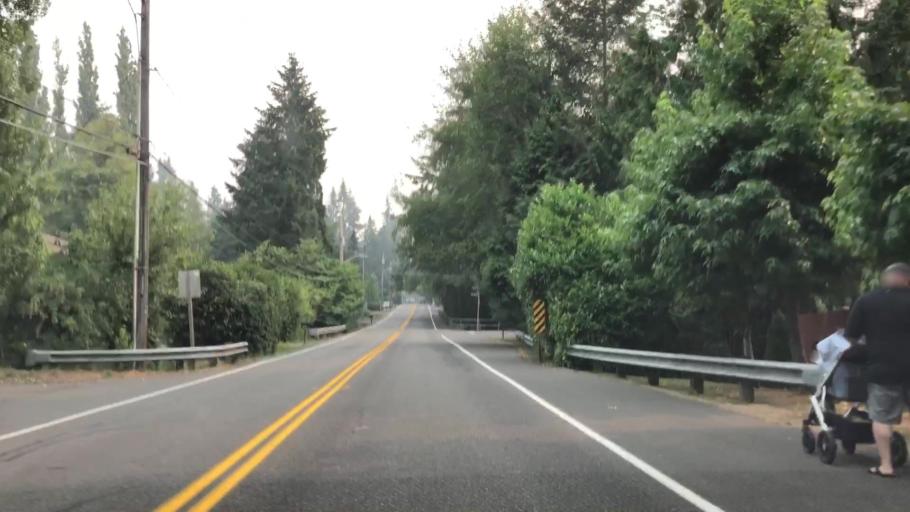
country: US
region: Washington
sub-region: King County
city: Lake Forest Park
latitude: 47.7670
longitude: -122.2920
